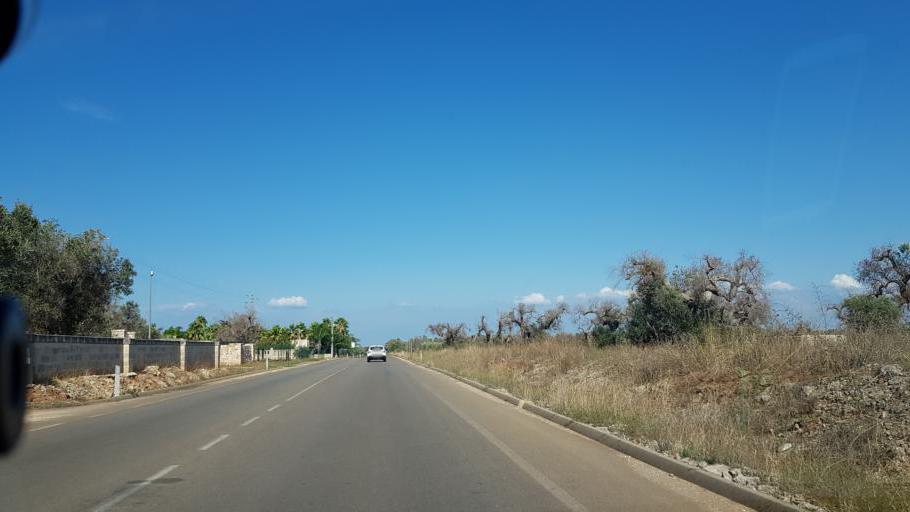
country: IT
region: Apulia
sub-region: Provincia di Lecce
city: Leverano
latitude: 40.2573
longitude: 17.9981
